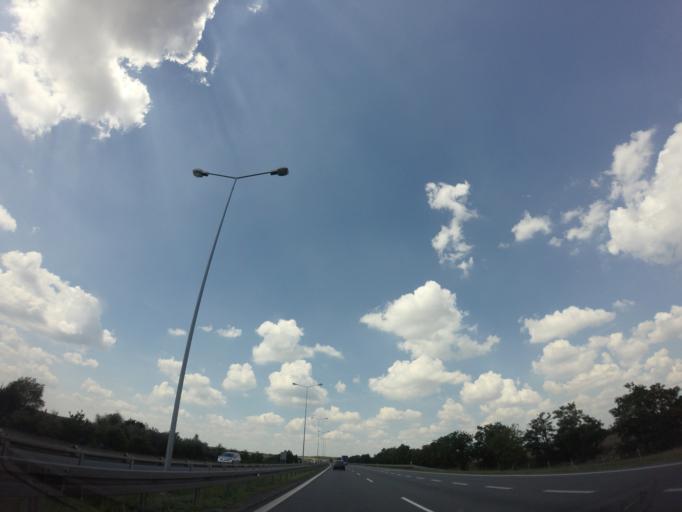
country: PL
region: Opole Voivodeship
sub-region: Powiat opolski
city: Proszkow
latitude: 50.5715
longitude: 17.8565
